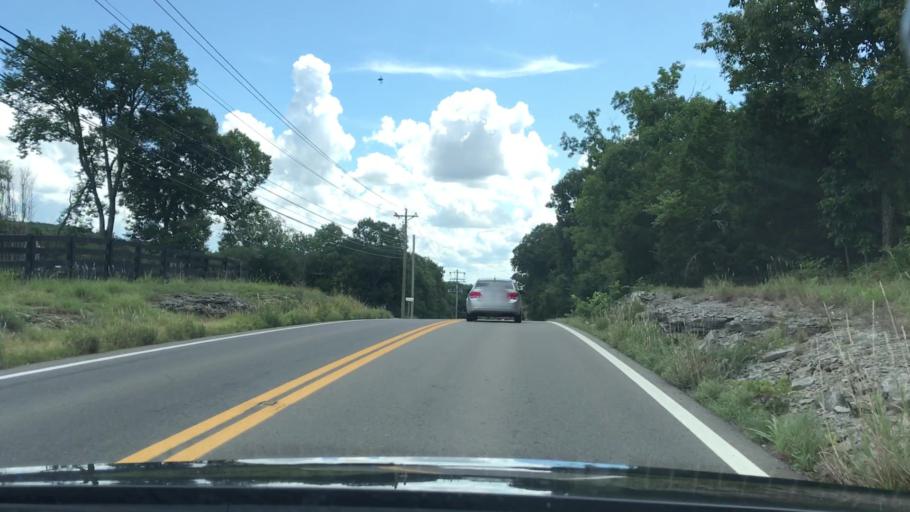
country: US
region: Tennessee
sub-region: Rutherford County
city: Smyrna
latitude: 35.8484
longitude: -86.5694
